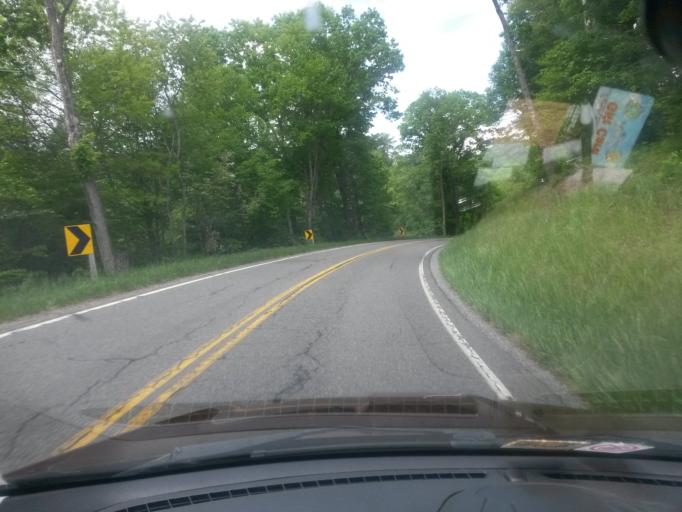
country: US
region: Virginia
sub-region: Floyd County
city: Floyd
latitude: 36.8930
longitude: -80.3251
